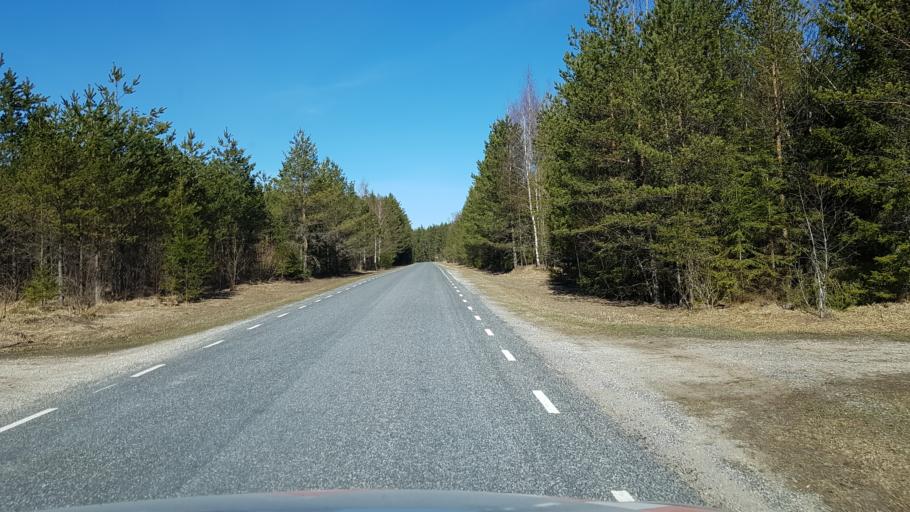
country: EE
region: Laeaene-Virumaa
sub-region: Vinni vald
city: Vinni
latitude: 59.1354
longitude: 26.5249
